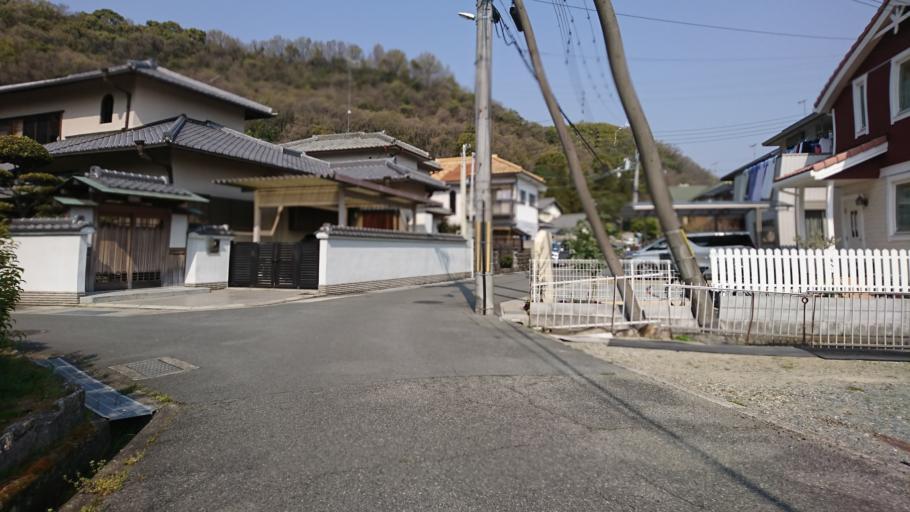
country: JP
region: Hyogo
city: Shirahamacho-usazakiminami
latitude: 34.7857
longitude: 134.7662
